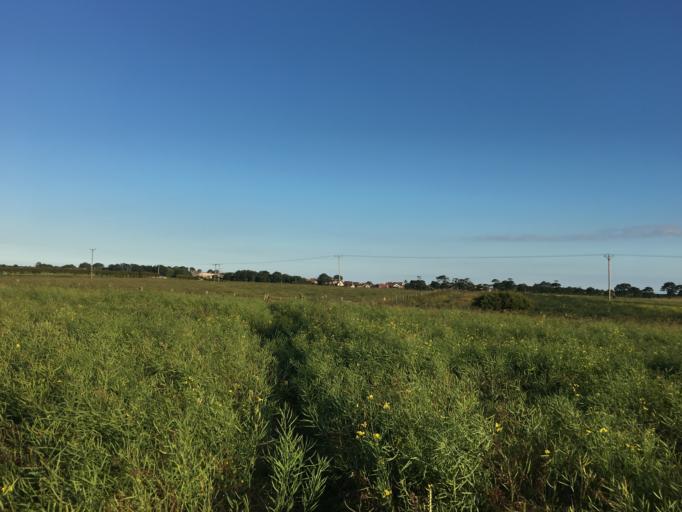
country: GB
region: England
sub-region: Northumberland
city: North Sunderland
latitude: 55.5824
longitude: -1.6732
